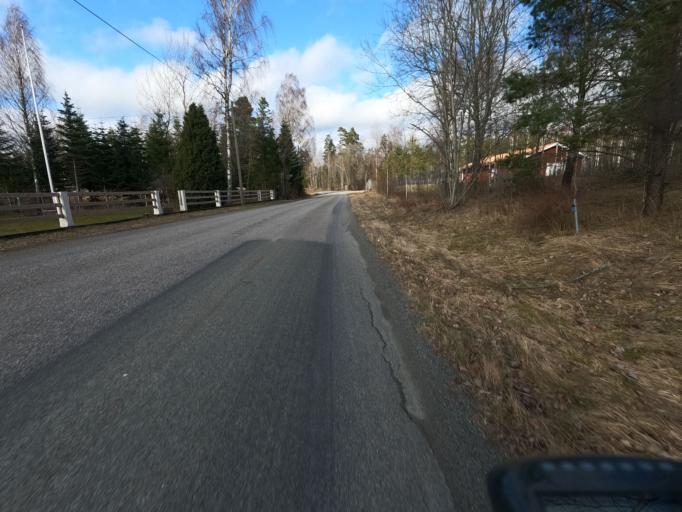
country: SE
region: Kronoberg
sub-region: Alvesta Kommun
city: Vislanda
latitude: 56.7887
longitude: 14.4838
